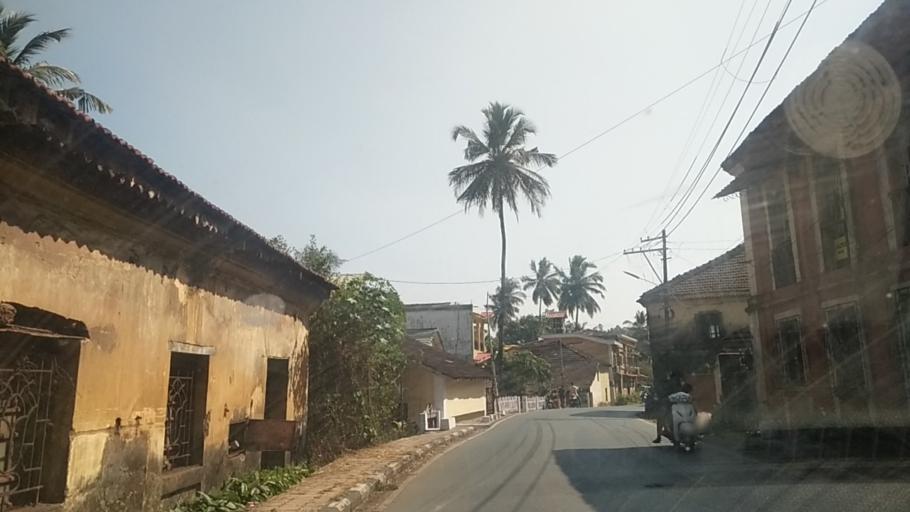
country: IN
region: Goa
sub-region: North Goa
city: Panaji
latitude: 15.5048
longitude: 73.8673
